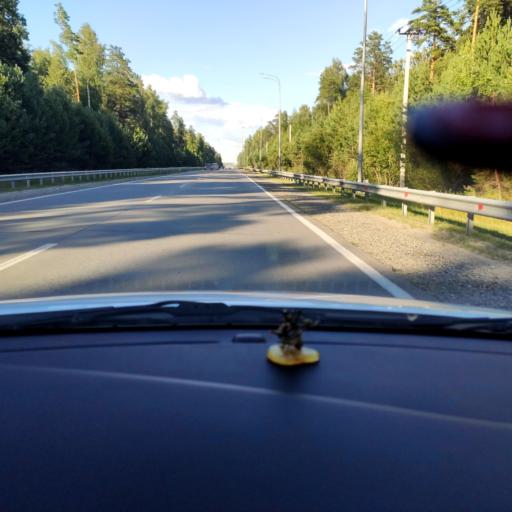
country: RU
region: Tatarstan
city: Stolbishchi
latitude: 55.6576
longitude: 49.1491
